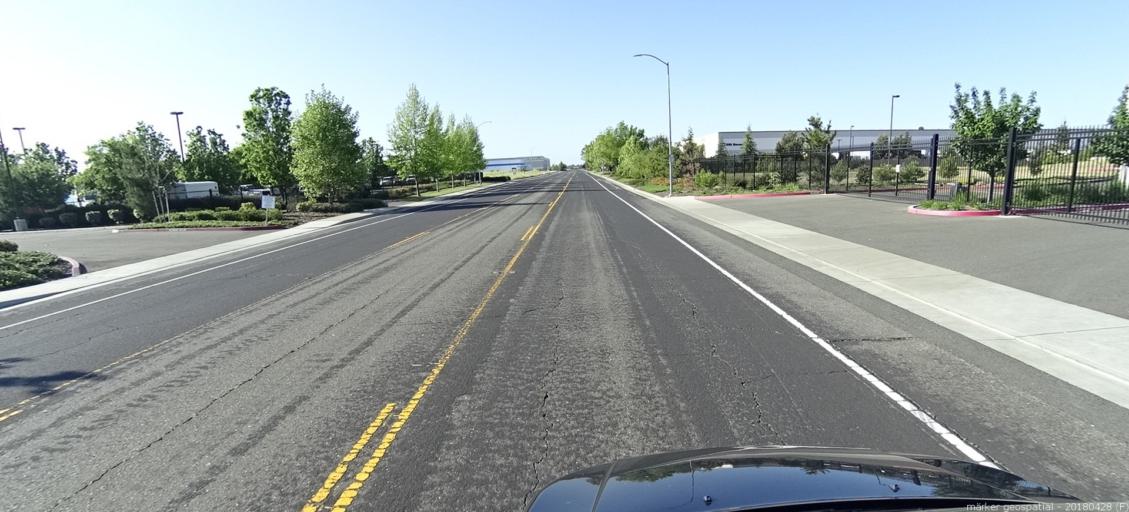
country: US
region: California
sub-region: Yolo County
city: West Sacramento
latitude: 38.5535
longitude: -121.5629
